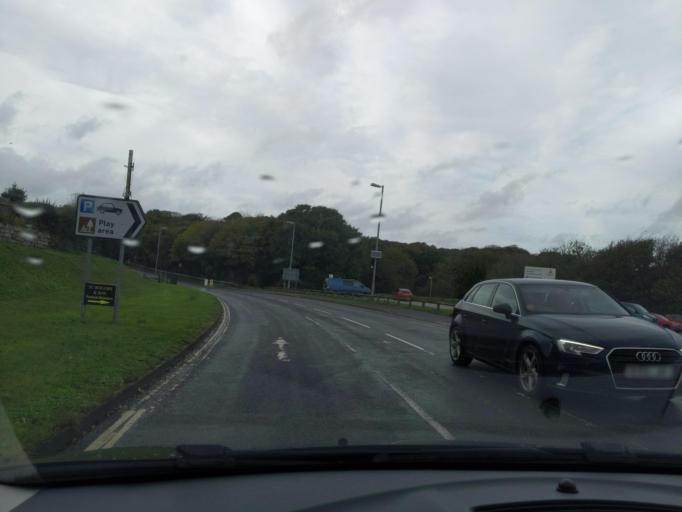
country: GB
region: England
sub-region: Cornwall
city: Padstow
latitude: 50.5396
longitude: -4.9420
